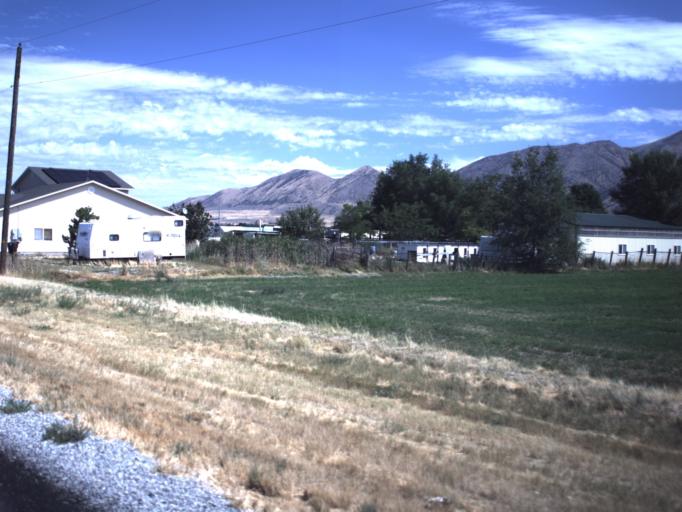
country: US
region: Utah
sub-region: Box Elder County
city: Elwood
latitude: 41.6649
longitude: -112.1407
